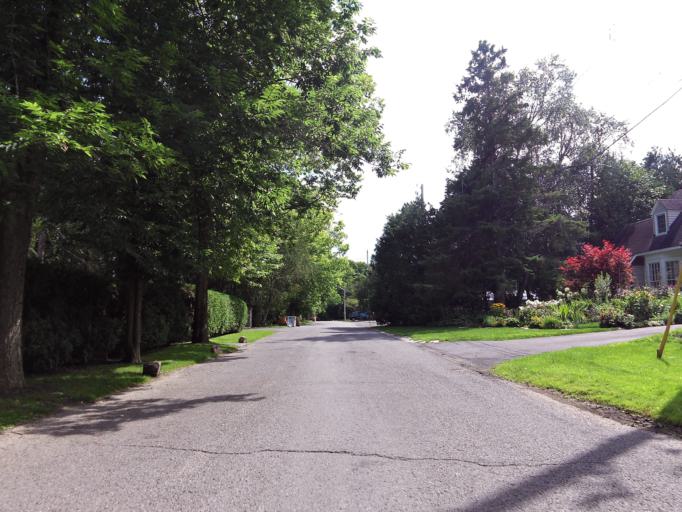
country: CA
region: Quebec
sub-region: Outaouais
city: Gatineau
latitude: 45.4532
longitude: -75.6724
